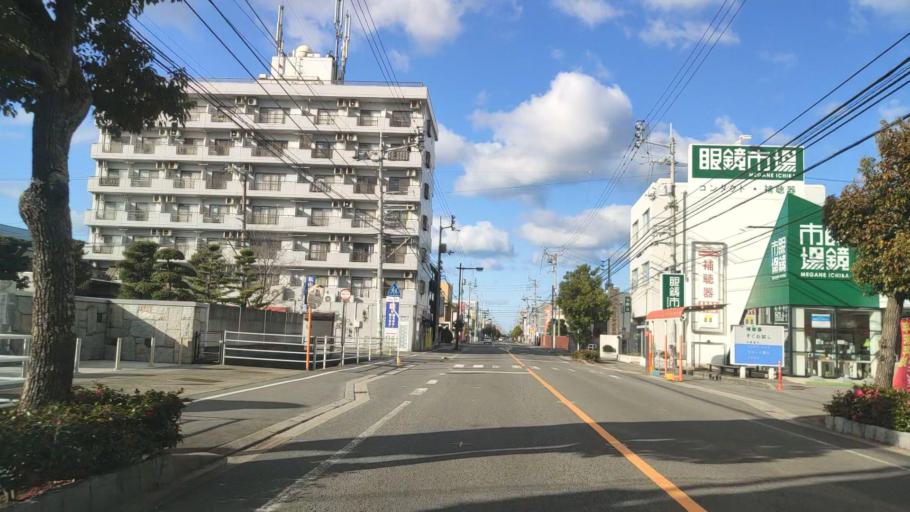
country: JP
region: Ehime
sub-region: Shikoku-chuo Shi
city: Matsuyama
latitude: 33.8284
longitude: 132.7388
